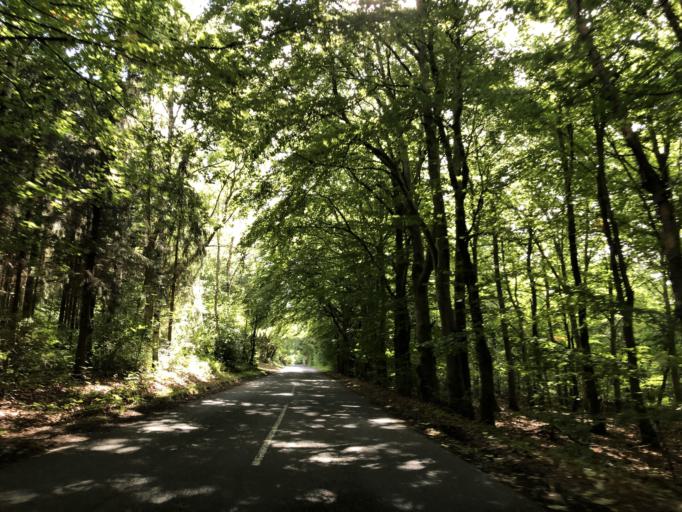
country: DK
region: North Denmark
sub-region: Vesthimmerland Kommune
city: Alestrup
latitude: 56.6076
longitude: 9.4338
